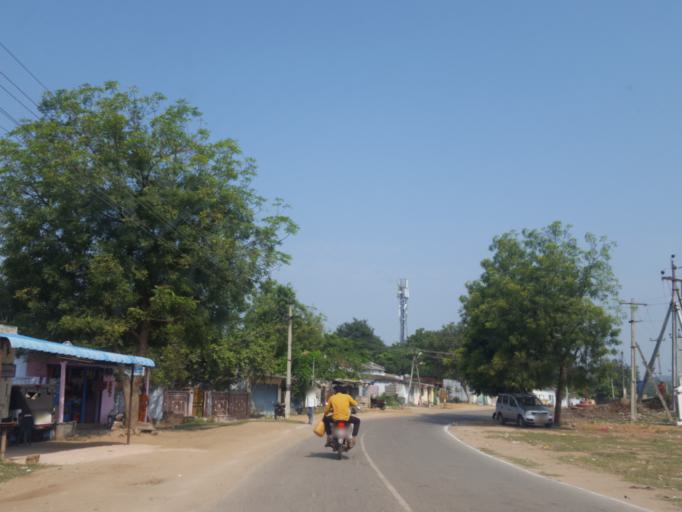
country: IN
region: Telangana
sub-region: Khammam
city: Yellandu
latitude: 17.6033
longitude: 80.3158
